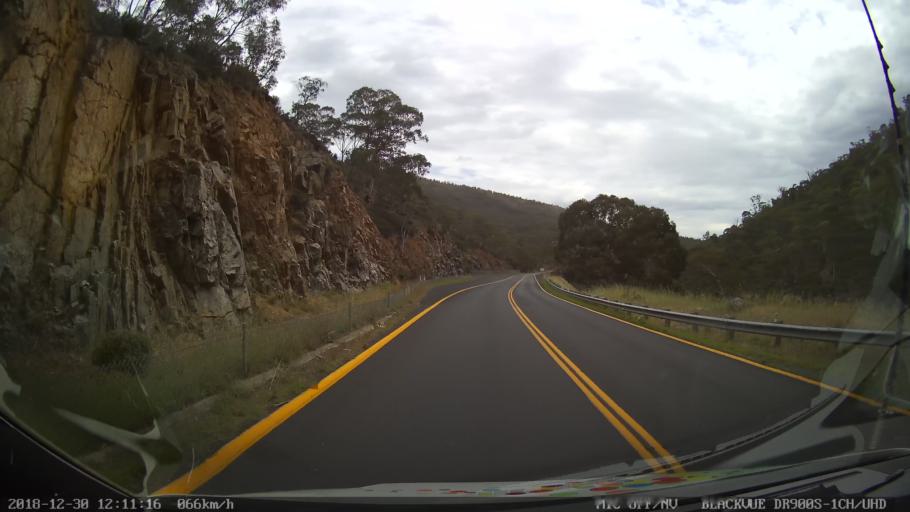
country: AU
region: New South Wales
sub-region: Snowy River
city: Jindabyne
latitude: -36.3681
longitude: 148.5891
